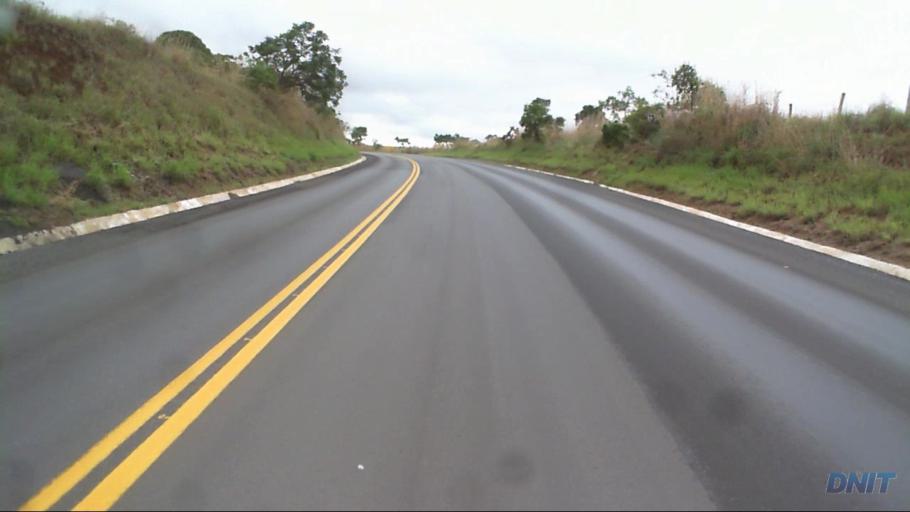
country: BR
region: Goias
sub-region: Padre Bernardo
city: Padre Bernardo
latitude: -15.2209
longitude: -48.5259
